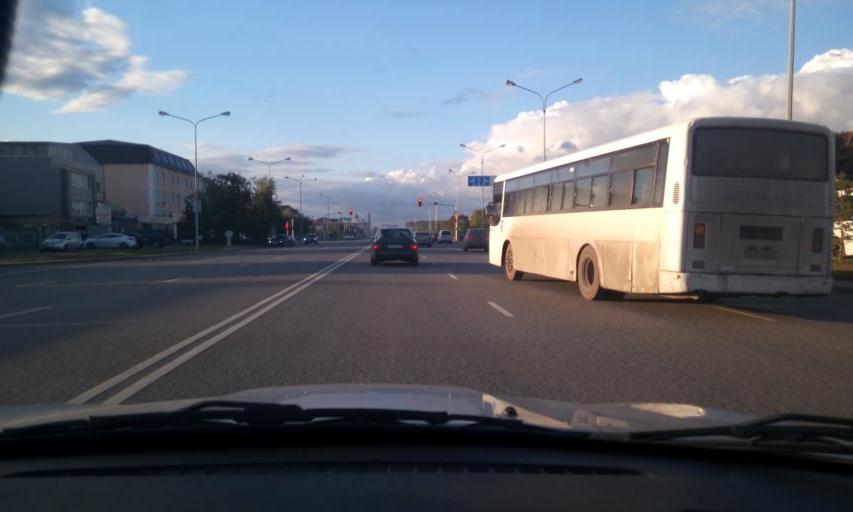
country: KZ
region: Astana Qalasy
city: Astana
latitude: 51.1361
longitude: 71.4922
